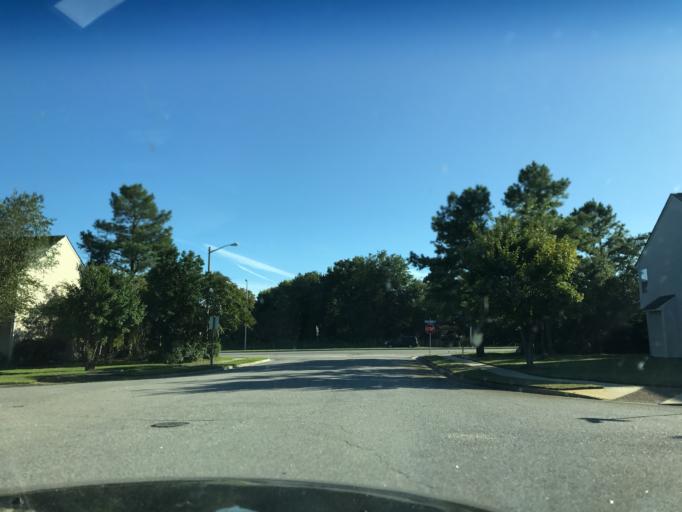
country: US
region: Virginia
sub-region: City of Chesapeake
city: Chesapeake
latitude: 36.7290
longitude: -76.3040
